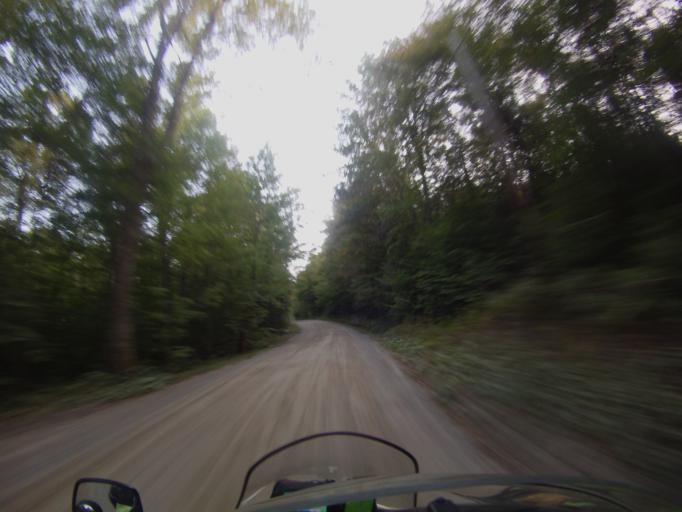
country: US
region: Vermont
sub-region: Addison County
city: Bristol
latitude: 44.0171
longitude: -73.0263
